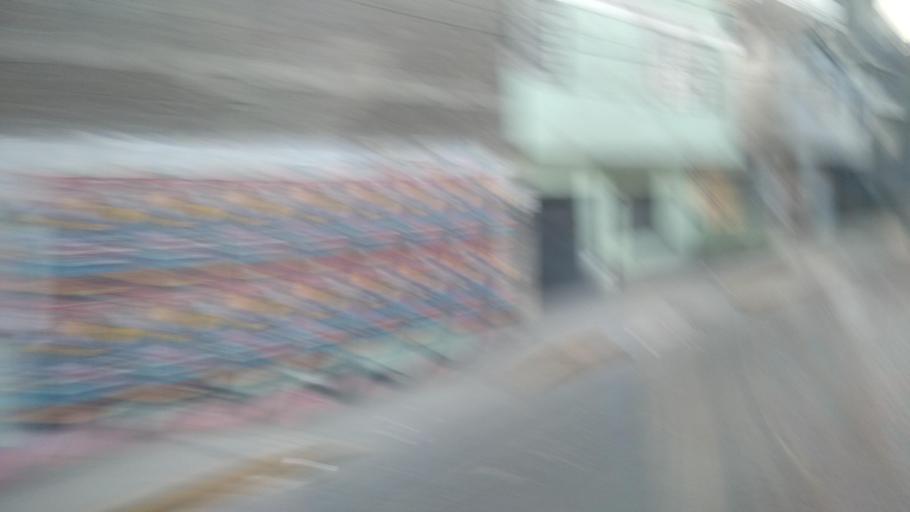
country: PE
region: Lima
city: Lima
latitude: -12.0186
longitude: -77.0007
